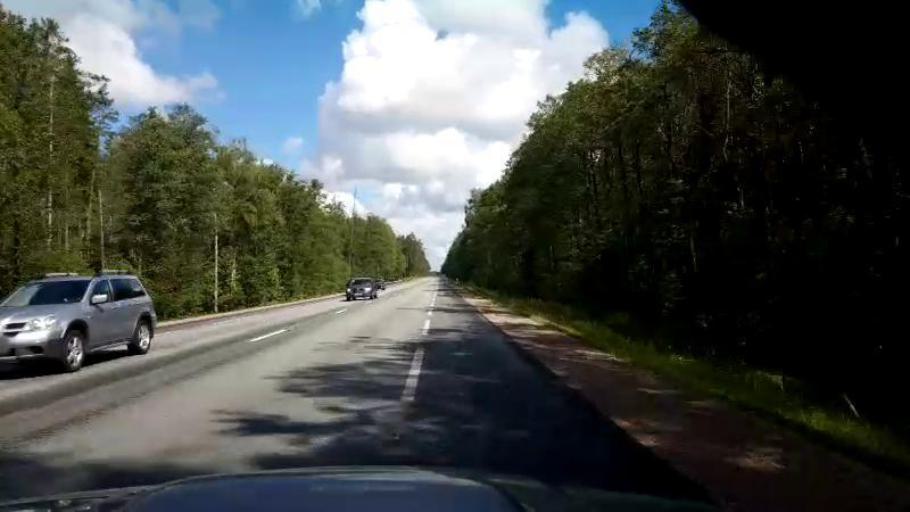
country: LV
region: Kekava
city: Kekava
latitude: 56.7430
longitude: 24.2513
